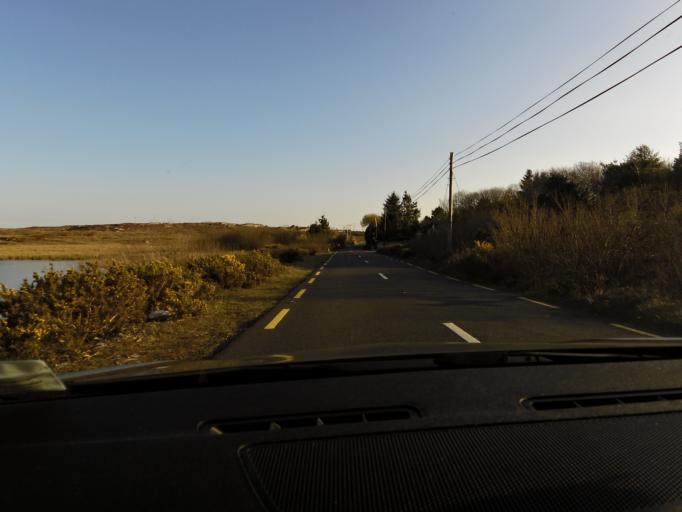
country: IE
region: Connaught
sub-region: County Galway
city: Oughterard
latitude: 53.3699
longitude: -9.5433
